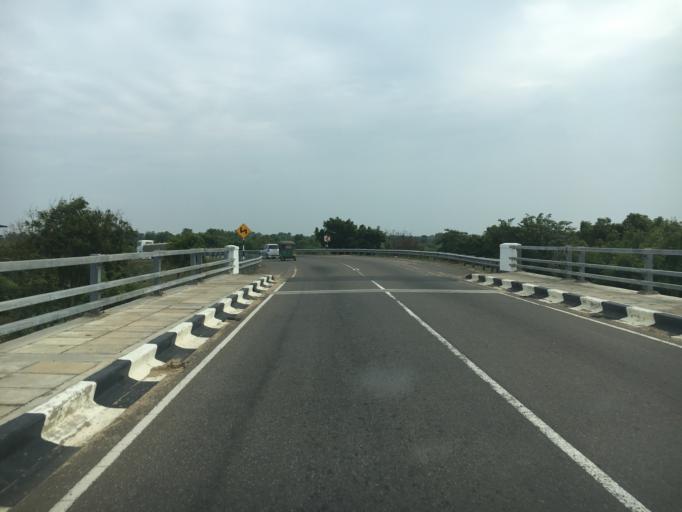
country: LK
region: Eastern Province
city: Trincomalee
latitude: 8.4690
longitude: 81.2030
